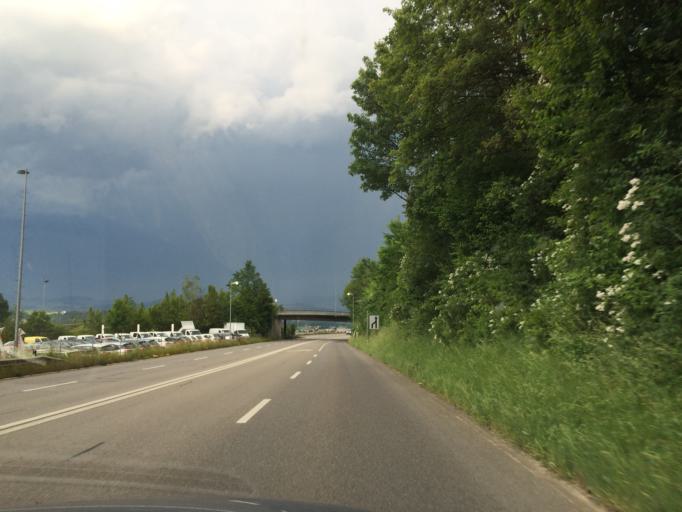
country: CH
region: Bern
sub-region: Bern-Mittelland District
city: Kehrsatz
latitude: 46.9068
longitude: 7.4746
